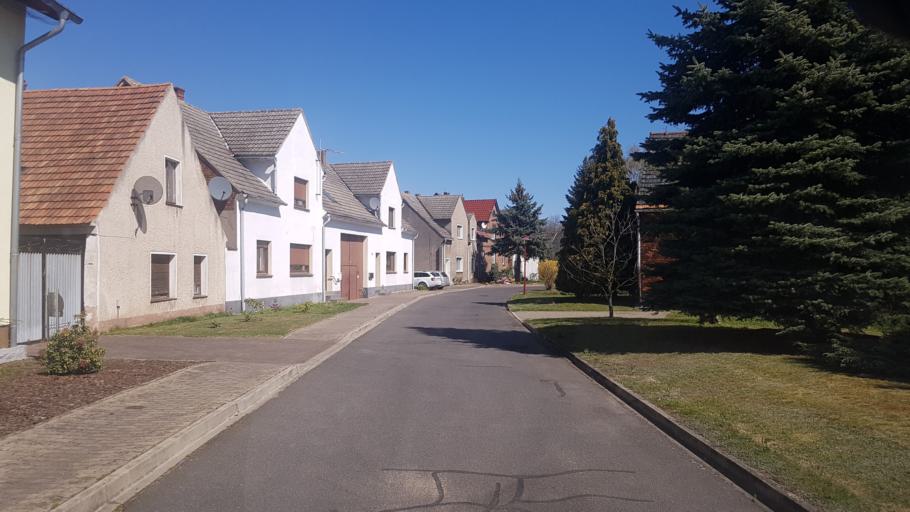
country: DE
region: Brandenburg
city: Sonnewalde
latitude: 51.7329
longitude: 13.6266
